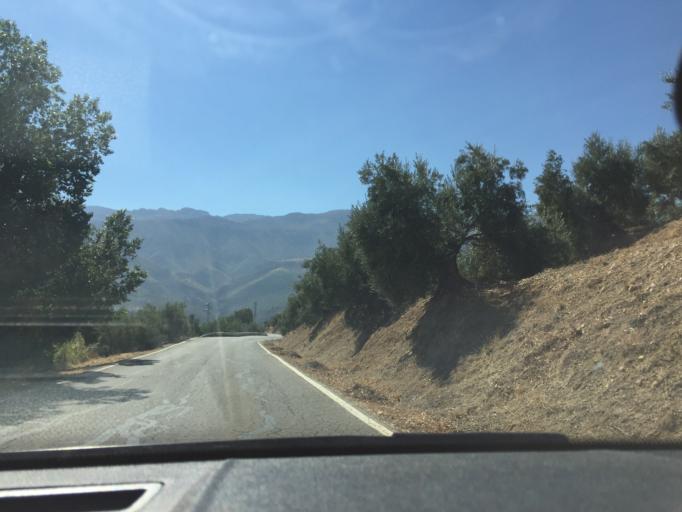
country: ES
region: Andalusia
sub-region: Provincia de Jaen
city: Jimena
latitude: 37.8109
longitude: -3.4589
